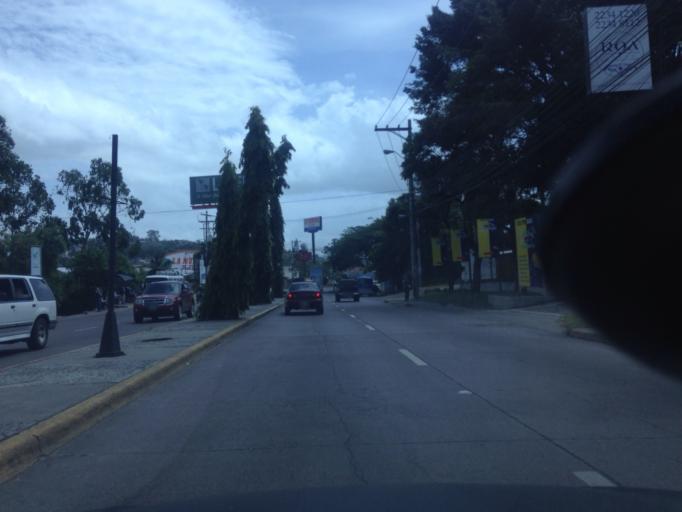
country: HN
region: Francisco Morazan
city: Tegucigalpa
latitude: 14.0634
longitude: -87.2192
